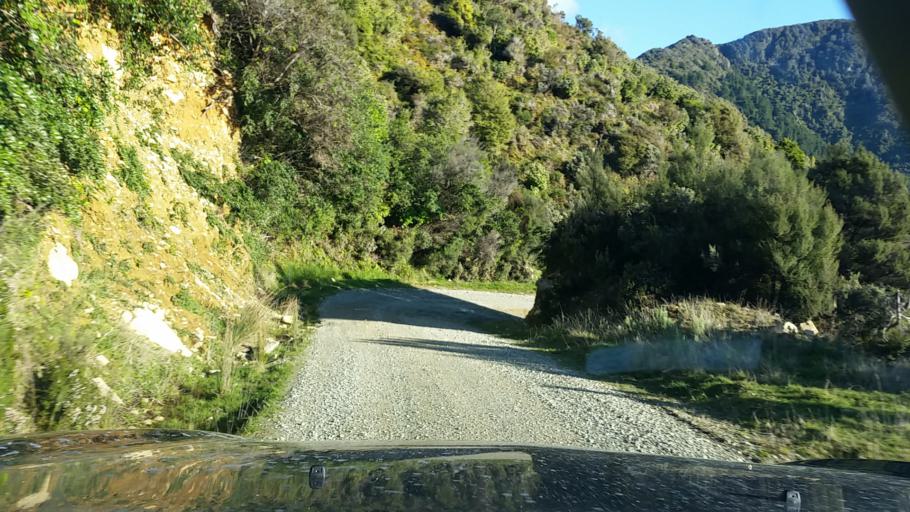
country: NZ
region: Marlborough
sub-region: Marlborough District
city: Picton
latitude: -41.0227
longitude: 174.1598
